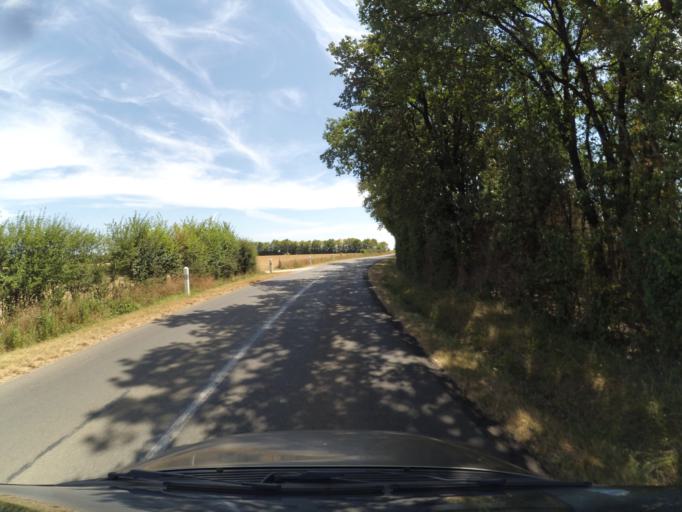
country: FR
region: Poitou-Charentes
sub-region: Departement de la Vienne
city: La Villedieu-du-Clain
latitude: 46.4076
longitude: 0.3405
